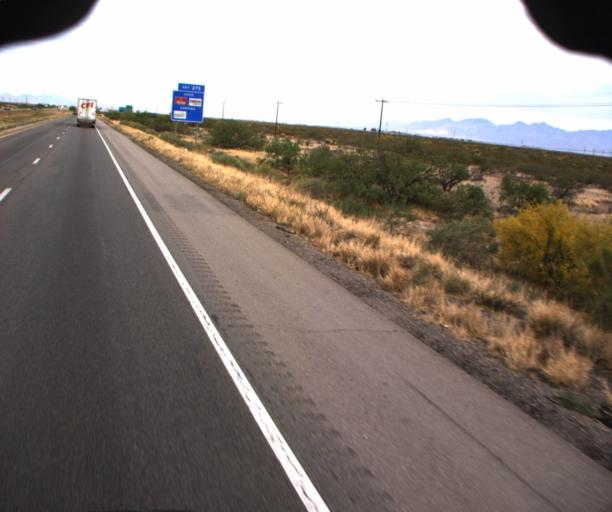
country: US
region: Arizona
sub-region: Pima County
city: Vail
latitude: 32.0494
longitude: -110.7540
